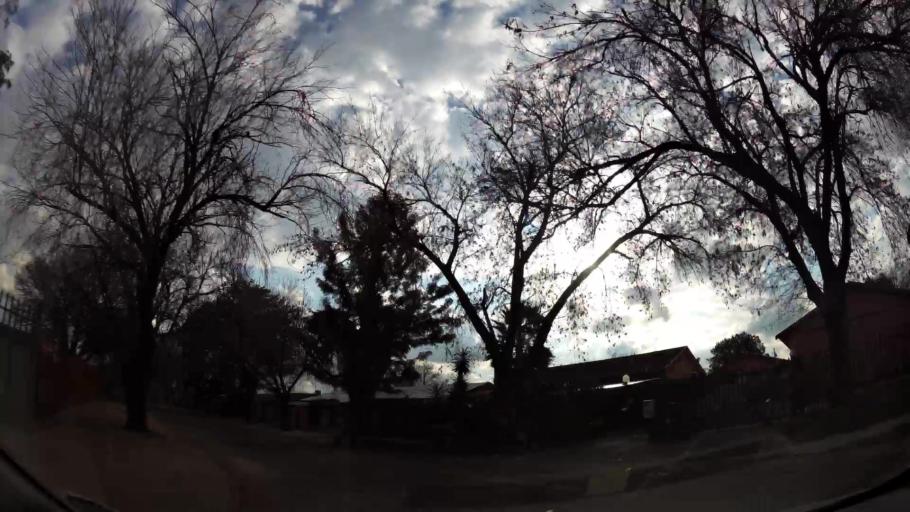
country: ZA
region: Orange Free State
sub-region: Fezile Dabi District Municipality
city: Sasolburg
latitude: -26.8245
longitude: 27.8284
